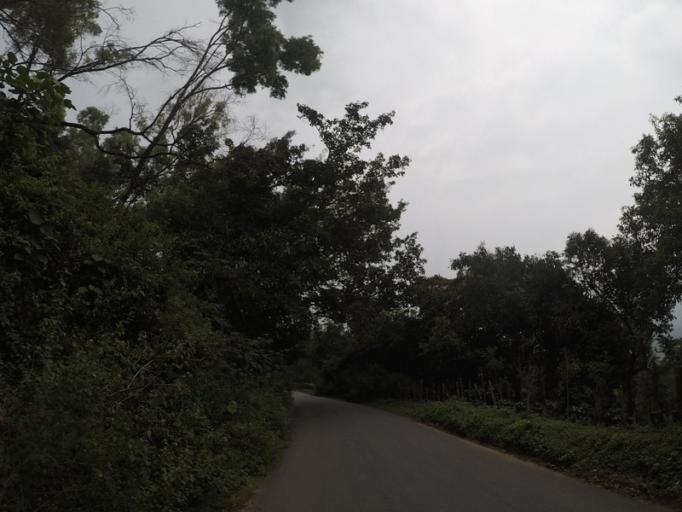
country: IN
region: Karnataka
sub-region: Chikmagalur
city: Mudigere
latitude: 13.1700
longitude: 75.4742
